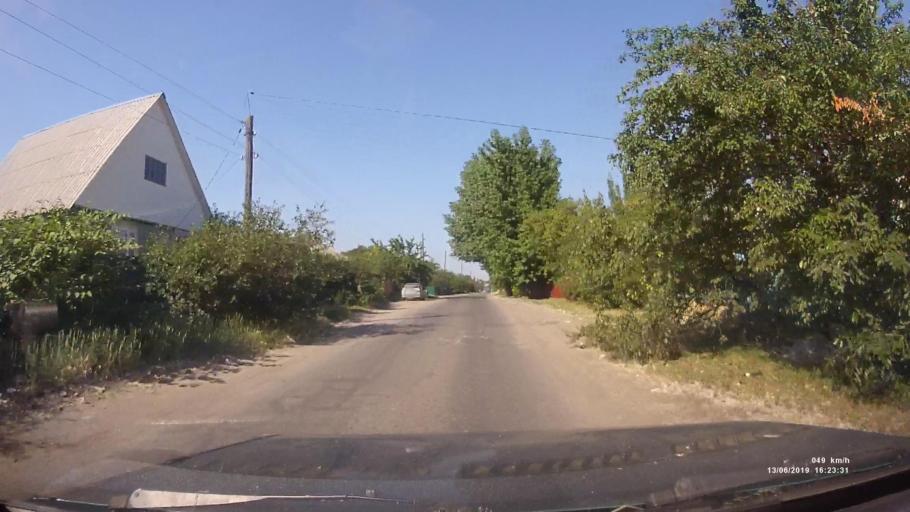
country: RU
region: Rostov
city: Kazanskaya
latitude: 49.7945
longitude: 41.1407
